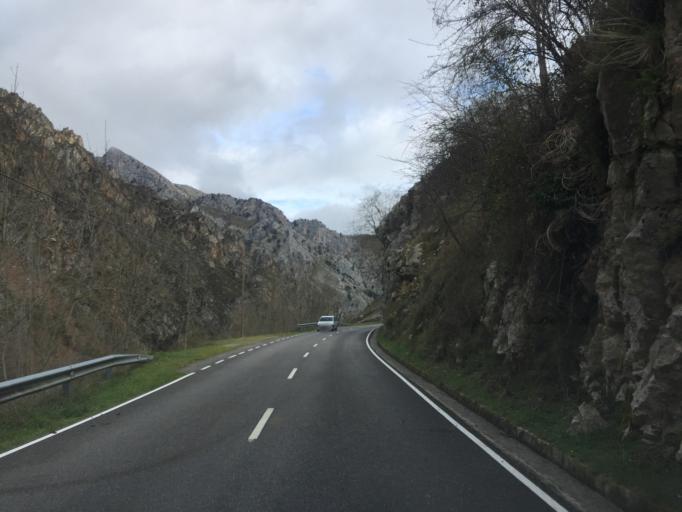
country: ES
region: Asturias
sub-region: Province of Asturias
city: Carrena
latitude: 43.2729
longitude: -4.8328
